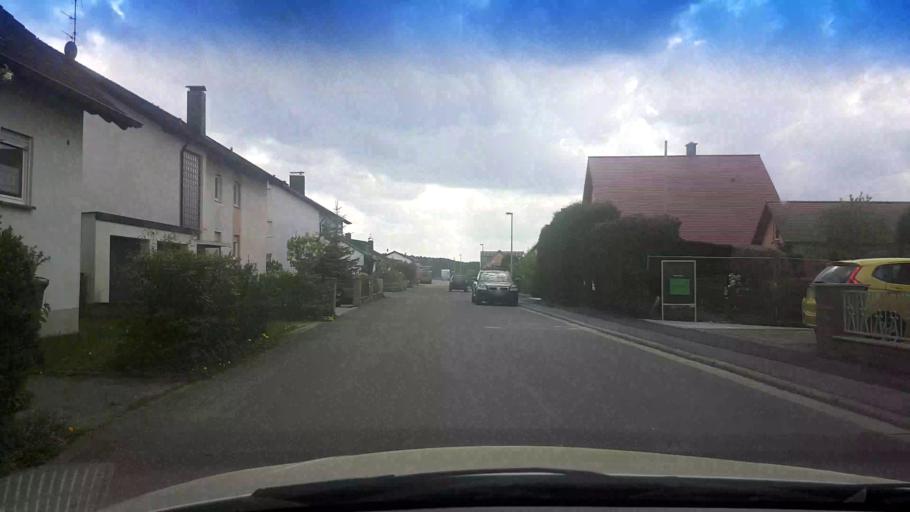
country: DE
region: Bavaria
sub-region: Upper Franconia
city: Pettstadt
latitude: 49.8265
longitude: 10.9243
